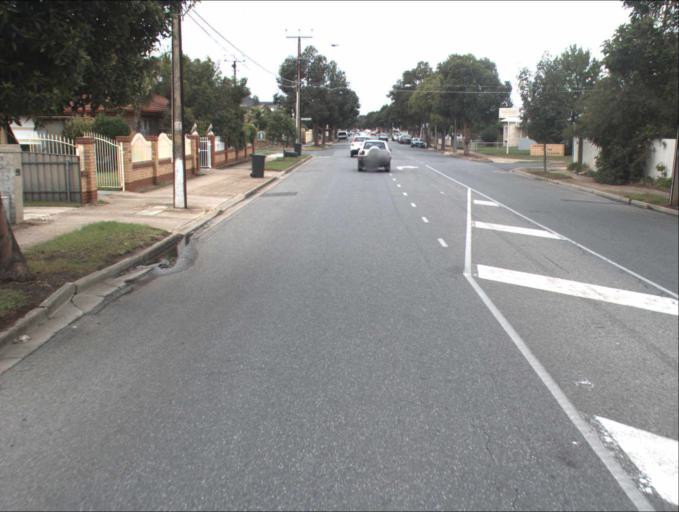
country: AU
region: South Australia
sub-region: Charles Sturt
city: Woodville
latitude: -34.8795
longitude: 138.5666
